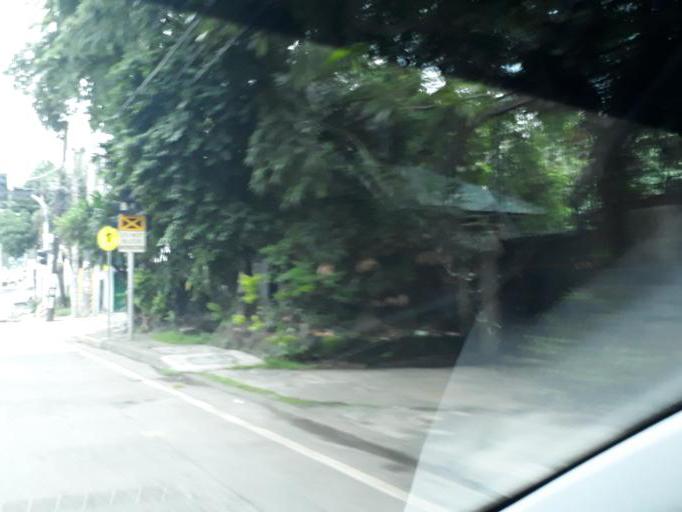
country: PH
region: Calabarzon
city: Del Monte
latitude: 14.6232
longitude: 121.0029
